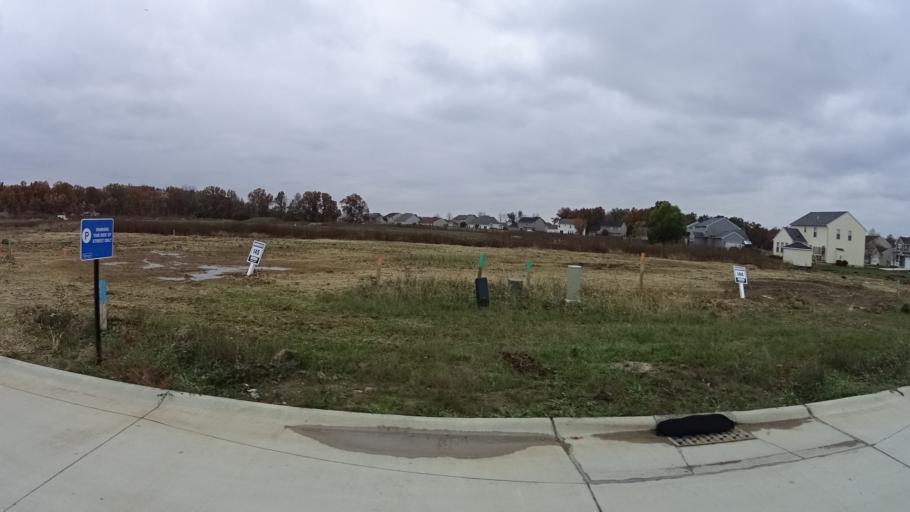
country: US
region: Ohio
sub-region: Lorain County
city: Lorain
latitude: 41.4403
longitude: -82.2179
